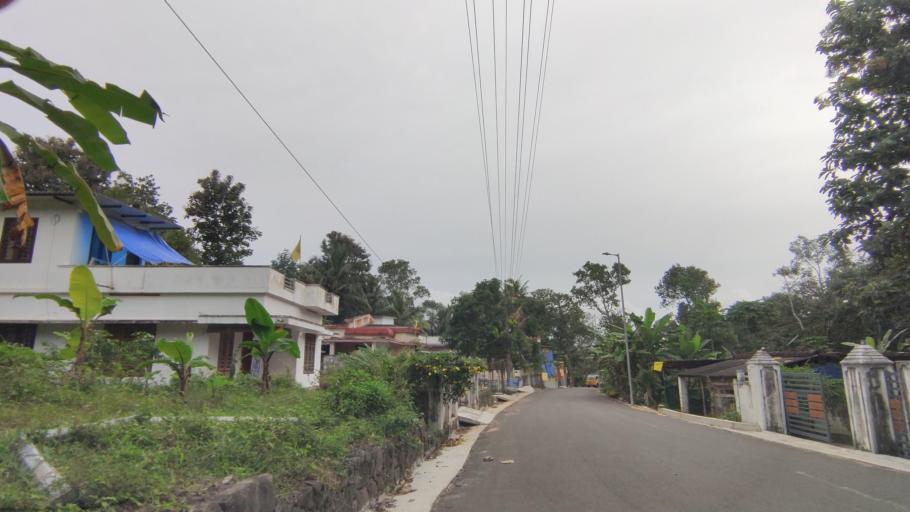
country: IN
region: Kerala
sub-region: Kottayam
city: Kottayam
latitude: 9.6643
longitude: 76.5175
